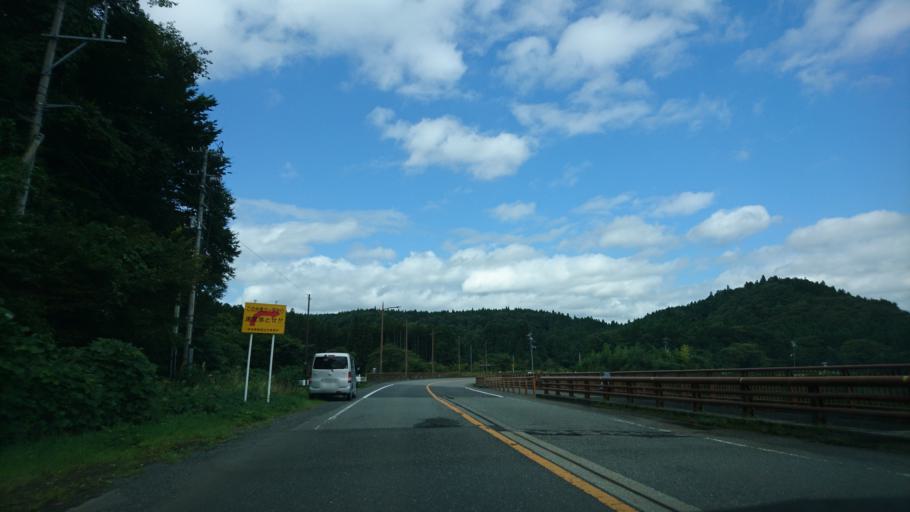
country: JP
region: Miyagi
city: Furukawa
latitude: 38.7778
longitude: 140.8529
